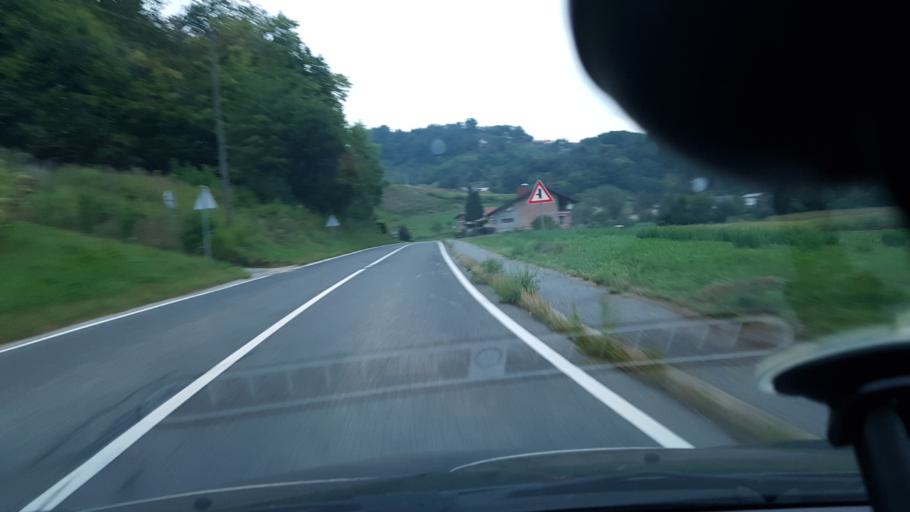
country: HR
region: Krapinsko-Zagorska
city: Pregrada
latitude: 46.2082
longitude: 15.7506
